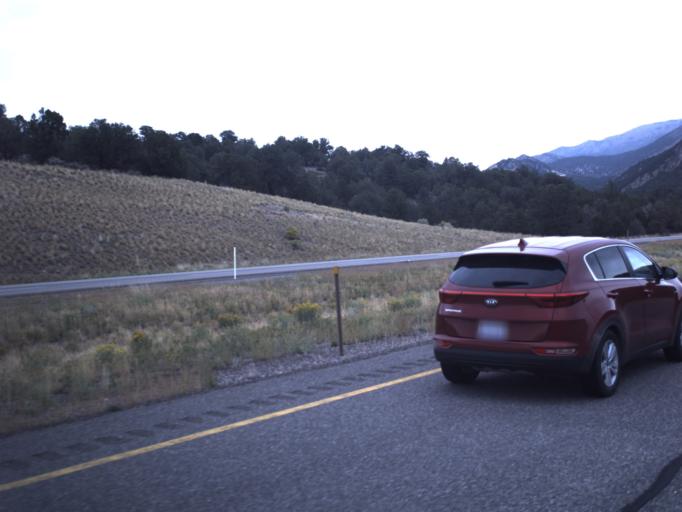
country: US
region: Utah
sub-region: Sevier County
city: Monroe
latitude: 38.5488
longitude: -112.3837
